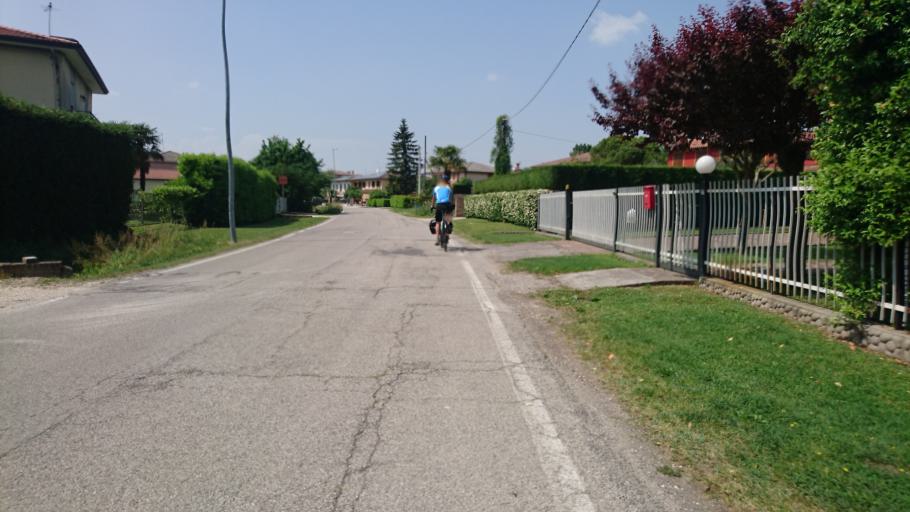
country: IT
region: Veneto
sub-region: Provincia di Venezia
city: Camponogara
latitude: 45.3733
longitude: 12.0979
